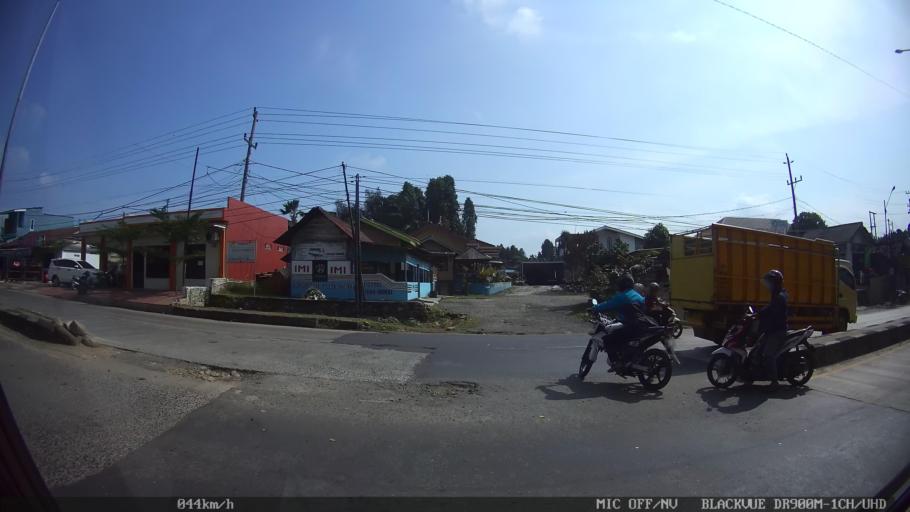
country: ID
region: Lampung
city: Kedaton
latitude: -5.3605
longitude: 105.2367
